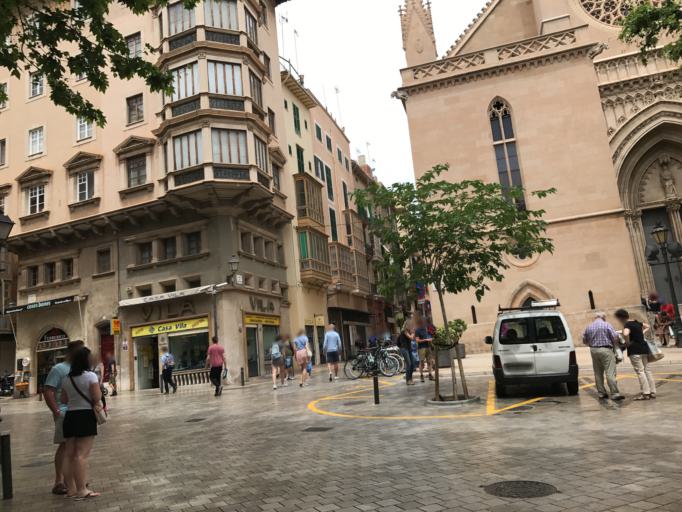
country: ES
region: Balearic Islands
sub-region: Illes Balears
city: Palma
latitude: 39.5691
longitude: 2.6508
